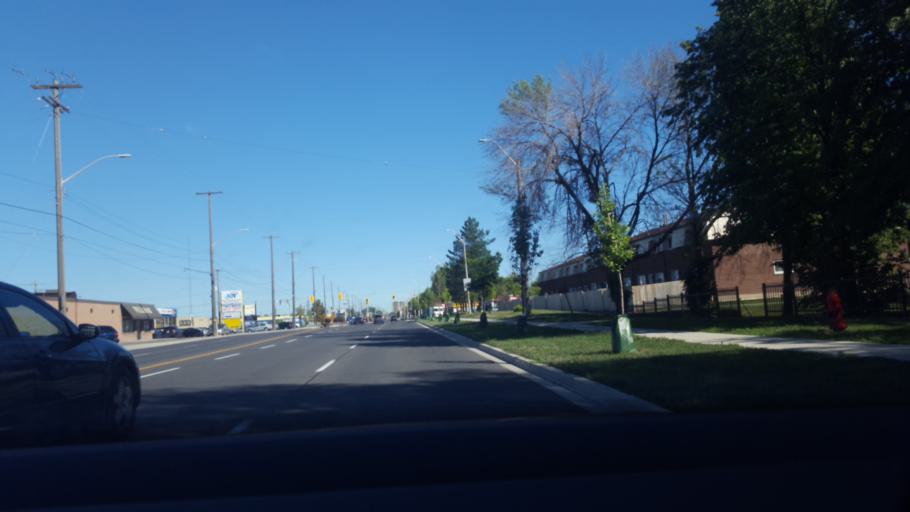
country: CA
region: Ontario
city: Hamilton
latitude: 43.2385
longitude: -79.7672
